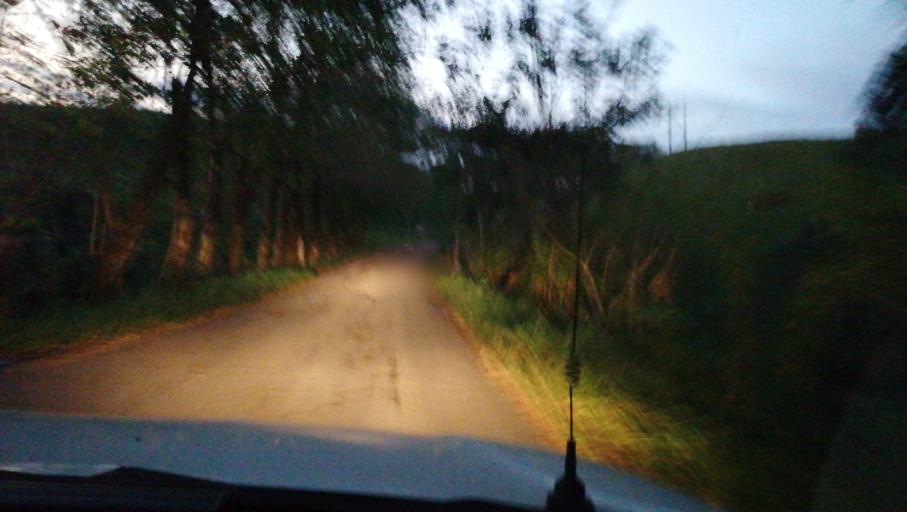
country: MX
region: Chiapas
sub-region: Ostuacan
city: Nuevo Juan del Grijalva
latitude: 17.4780
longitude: -93.3462
